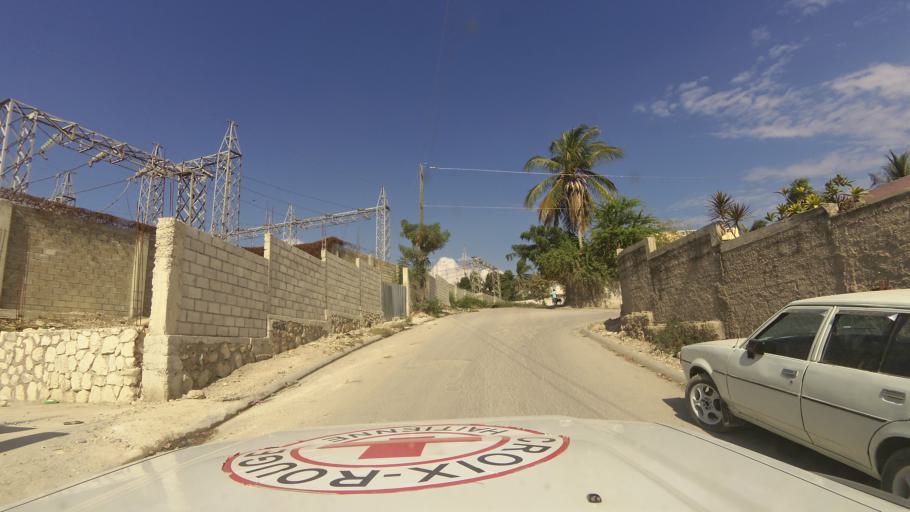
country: HT
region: Ouest
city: Delmas 73
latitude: 18.5595
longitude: -72.2920
